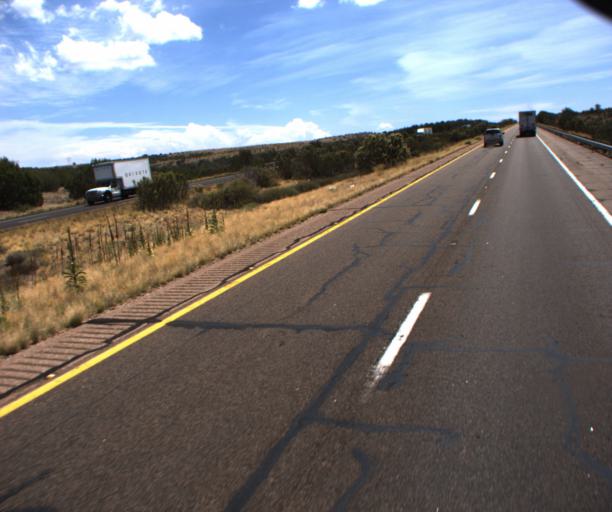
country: US
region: Arizona
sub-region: Yavapai County
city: Paulden
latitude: 35.2824
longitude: -112.7925
